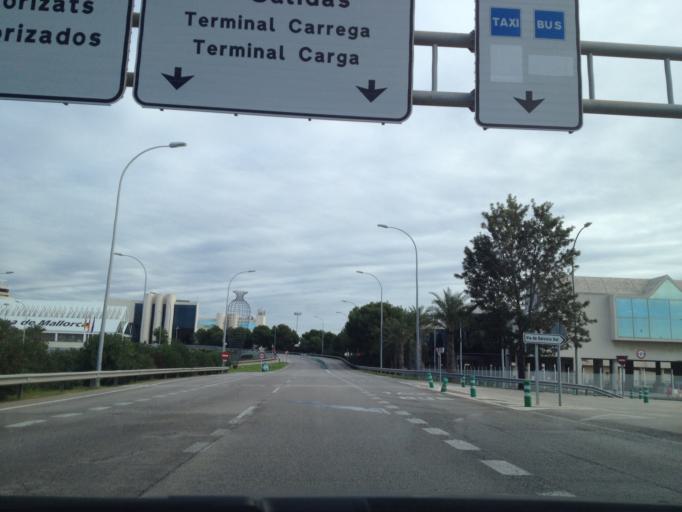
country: ES
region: Balearic Islands
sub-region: Illes Balears
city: s'Arenal
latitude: 39.5447
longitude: 2.7293
